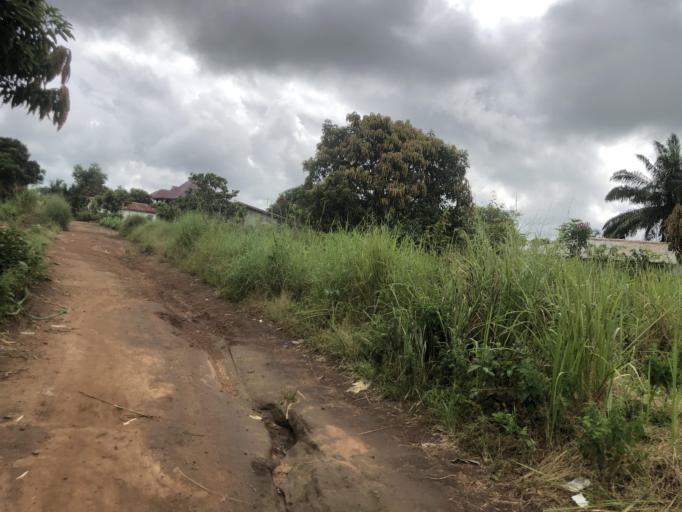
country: SL
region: Northern Province
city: Makeni
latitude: 8.9072
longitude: -12.0415
